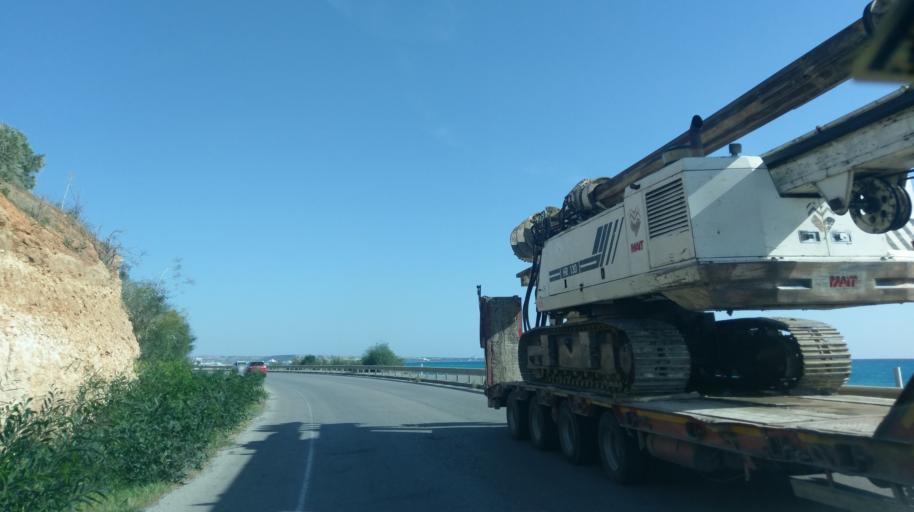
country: CY
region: Ammochostos
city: Trikomo
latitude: 35.3095
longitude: 33.9484
